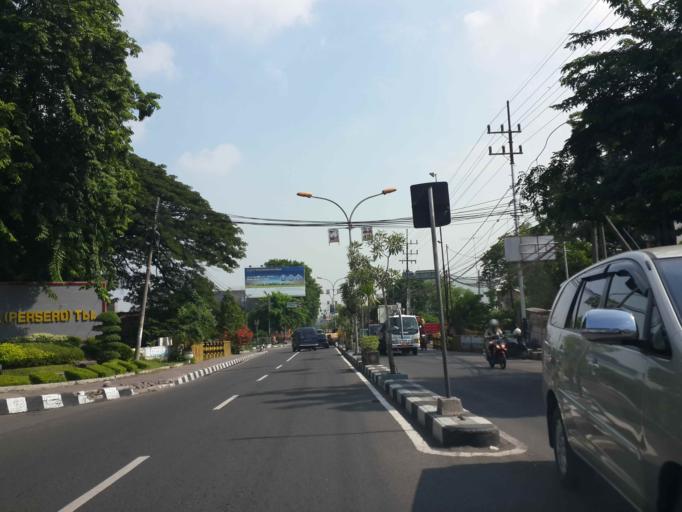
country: ID
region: East Java
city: Kebomas
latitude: -7.1755
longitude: 112.6518
